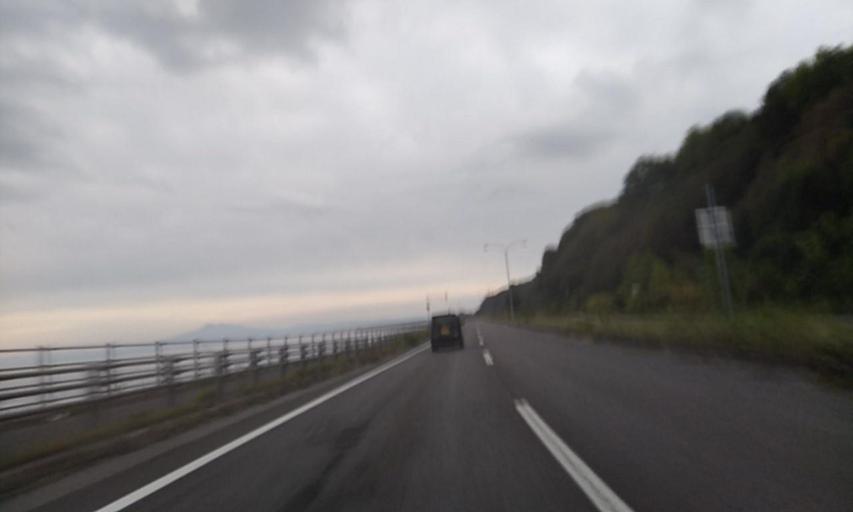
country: JP
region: Hokkaido
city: Abashiri
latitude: 44.0017
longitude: 144.2895
